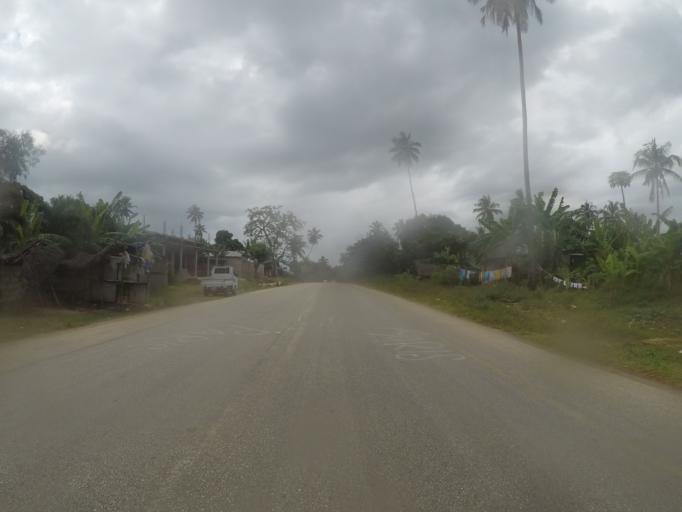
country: TZ
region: Zanzibar Central/South
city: Koani
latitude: -6.0491
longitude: 39.2241
